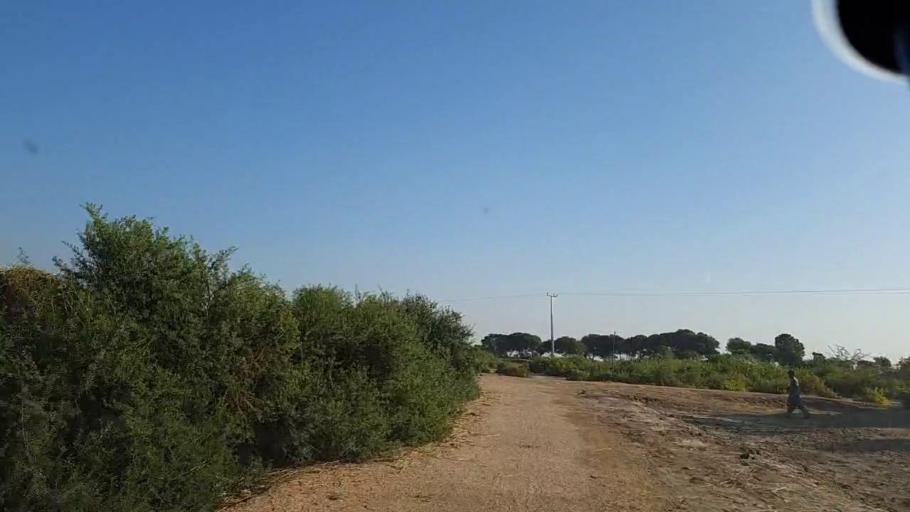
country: PK
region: Sindh
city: Chuhar Jamali
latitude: 24.5610
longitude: 68.0753
